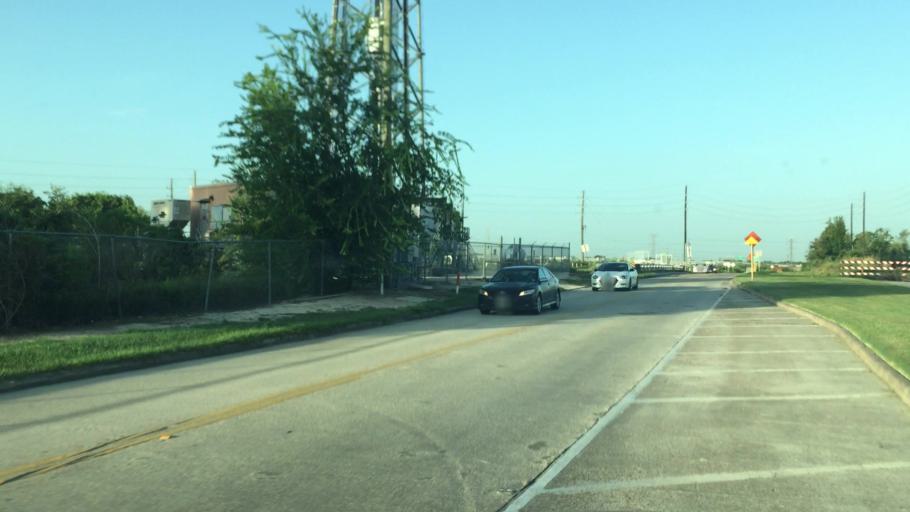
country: US
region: Texas
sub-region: Harris County
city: Hudson
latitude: 29.9455
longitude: -95.4734
